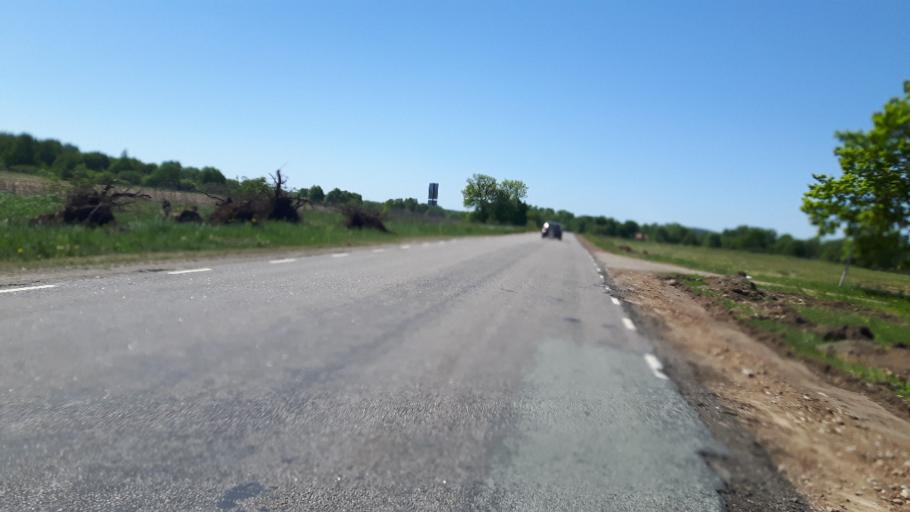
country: EE
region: Ida-Virumaa
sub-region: Narva-Joesuu linn
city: Narva-Joesuu
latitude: 59.3969
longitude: 27.9292
